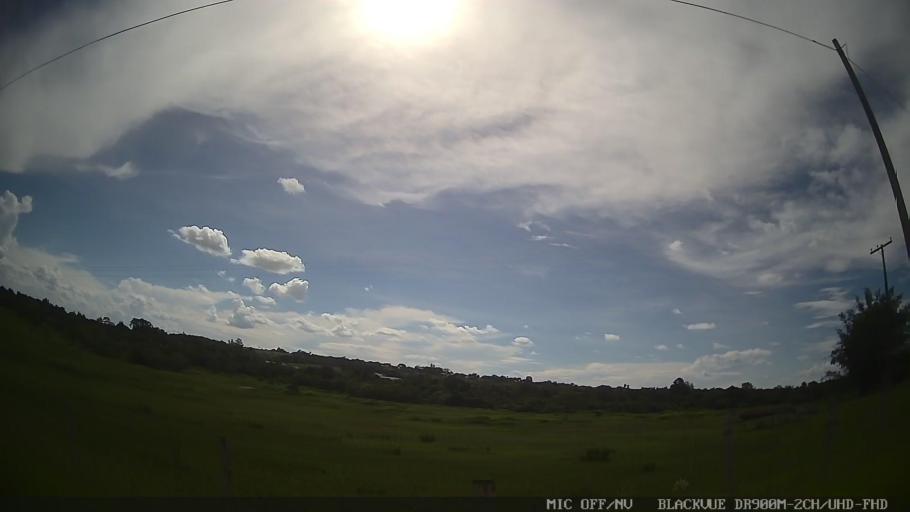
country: BR
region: Sao Paulo
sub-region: Conchas
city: Conchas
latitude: -23.0032
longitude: -48.0015
